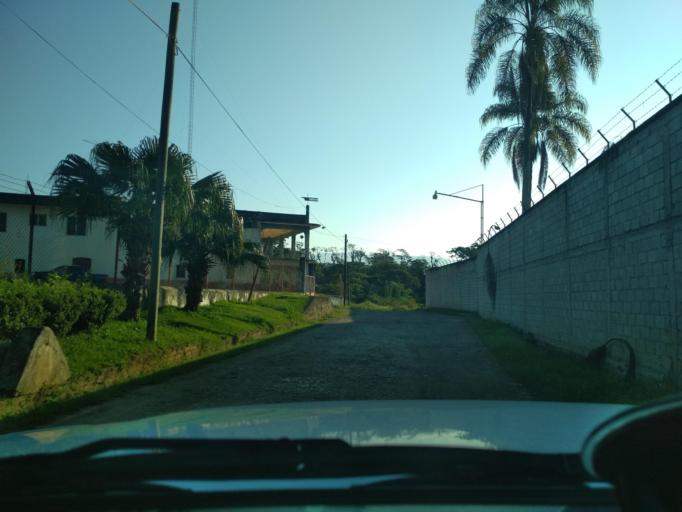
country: MX
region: Veracruz
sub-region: Fortin
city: Fraccionamiento Villas de la Llave
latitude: 18.9252
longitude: -96.9919
